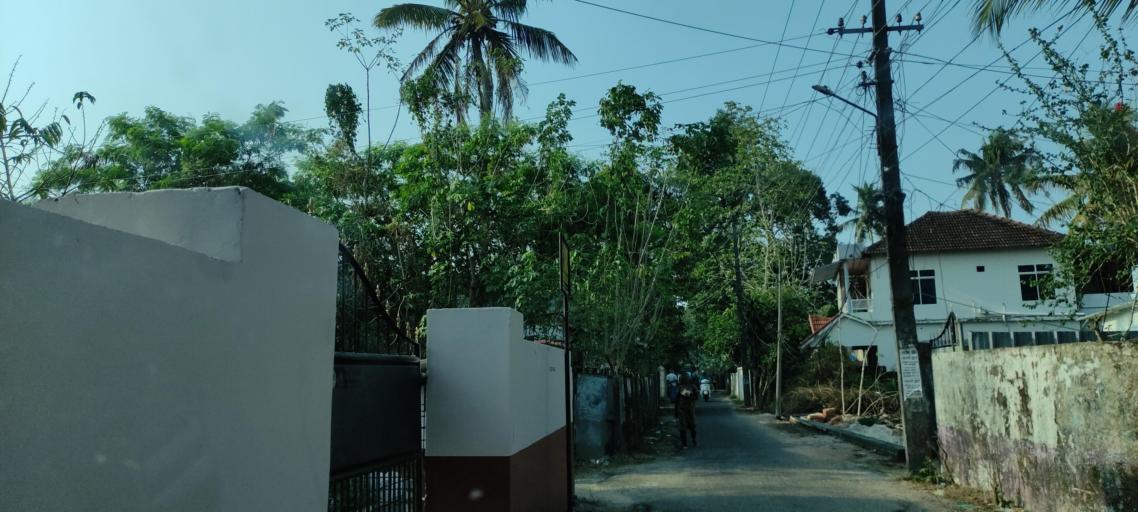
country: IN
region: Kerala
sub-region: Alappuzha
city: Alleppey
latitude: 9.5114
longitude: 76.3219
